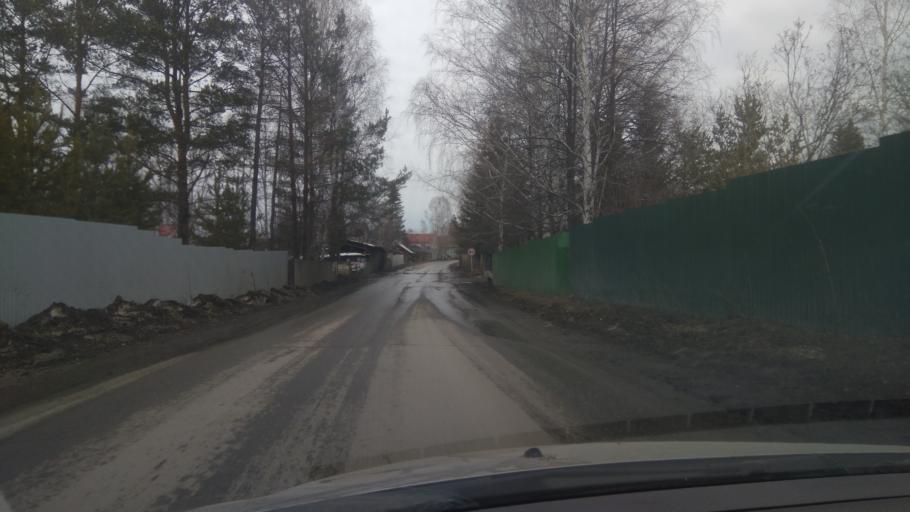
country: RU
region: Sverdlovsk
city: Severka
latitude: 56.8471
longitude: 60.3832
